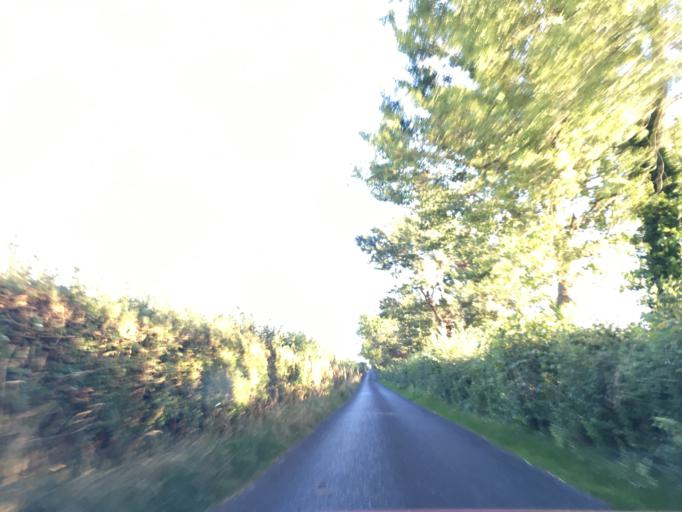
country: IE
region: Munster
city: Cashel
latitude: 52.5070
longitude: -7.9334
